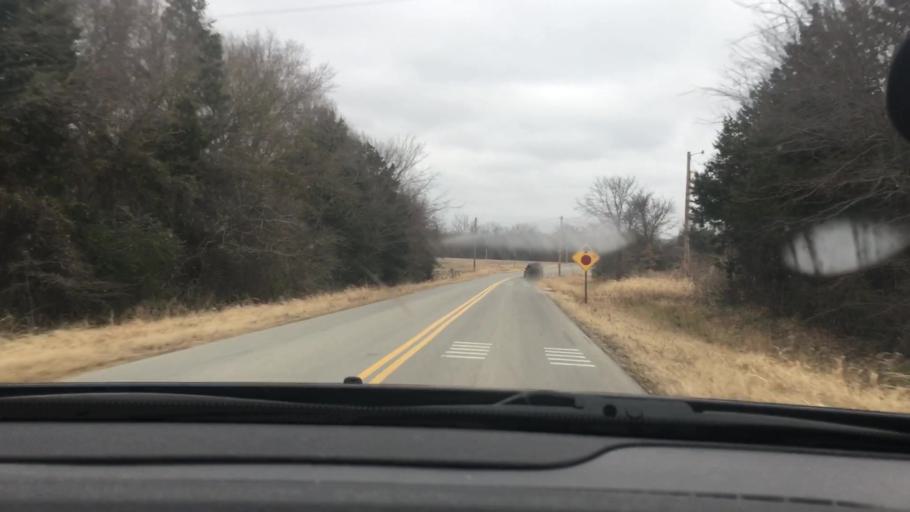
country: US
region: Oklahoma
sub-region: Atoka County
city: Atoka
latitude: 34.3433
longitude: -96.0754
